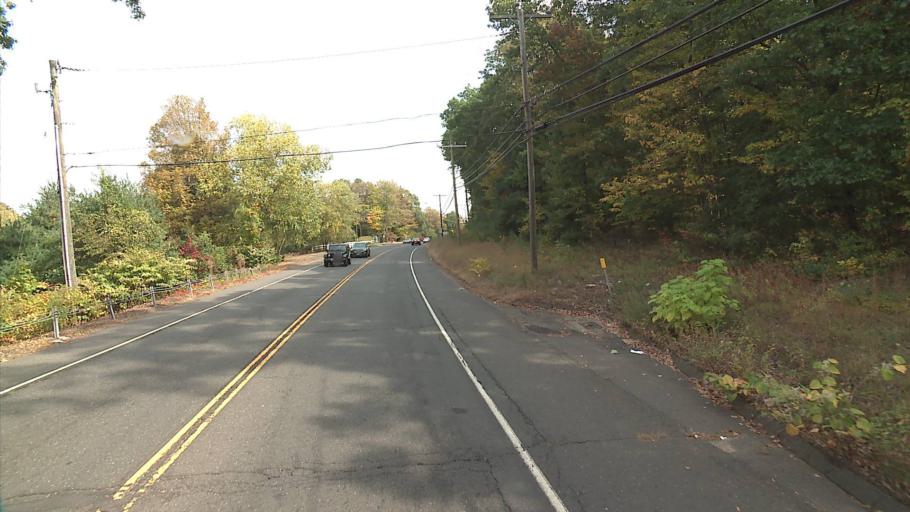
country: US
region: Connecticut
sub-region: Hartford County
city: Plainville
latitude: 41.7052
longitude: -72.8841
